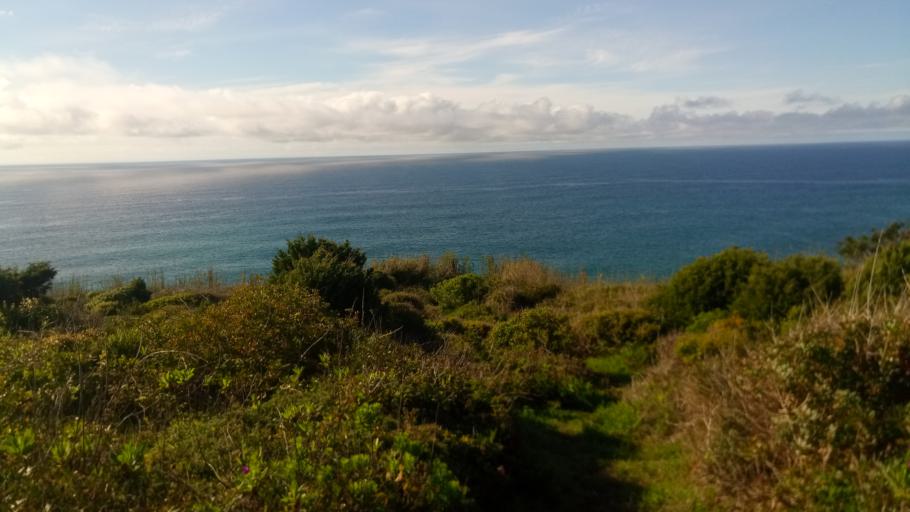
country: PT
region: Leiria
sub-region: Caldas da Rainha
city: Caldas da Rainha
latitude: 39.4943
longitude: -9.1732
